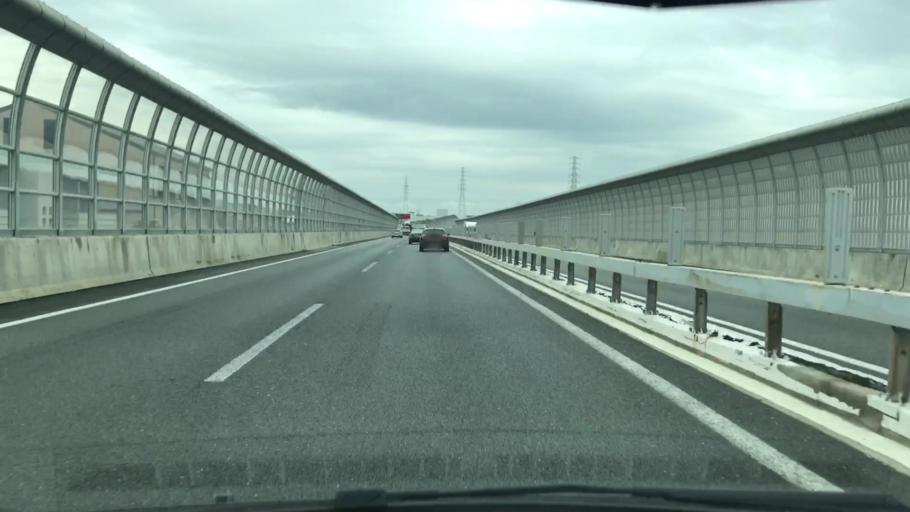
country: JP
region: Hyogo
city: Amagasaki
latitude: 34.7424
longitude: 135.4042
